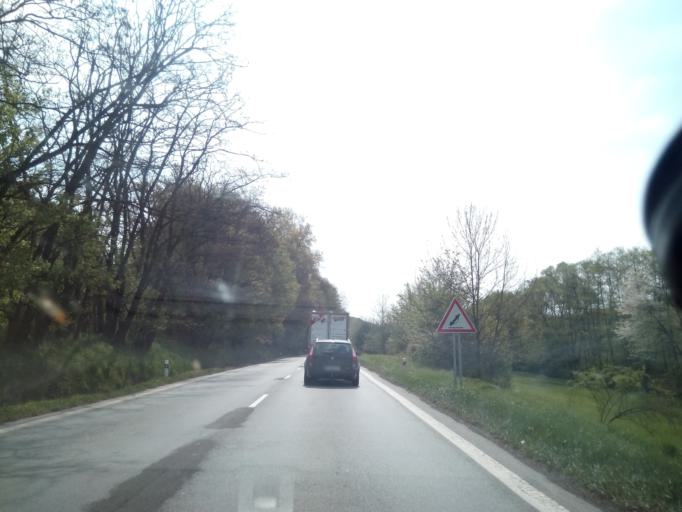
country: SK
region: Presovsky
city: Giraltovce
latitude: 49.0482
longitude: 21.4369
